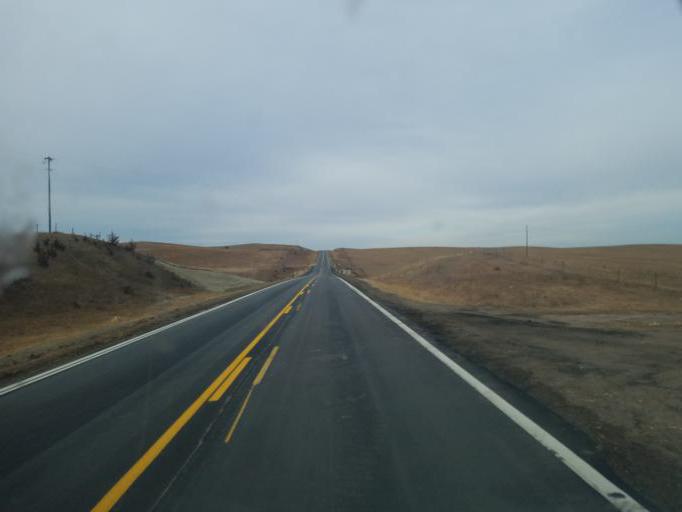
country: US
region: Nebraska
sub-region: Knox County
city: Center
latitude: 42.5970
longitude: -97.8258
